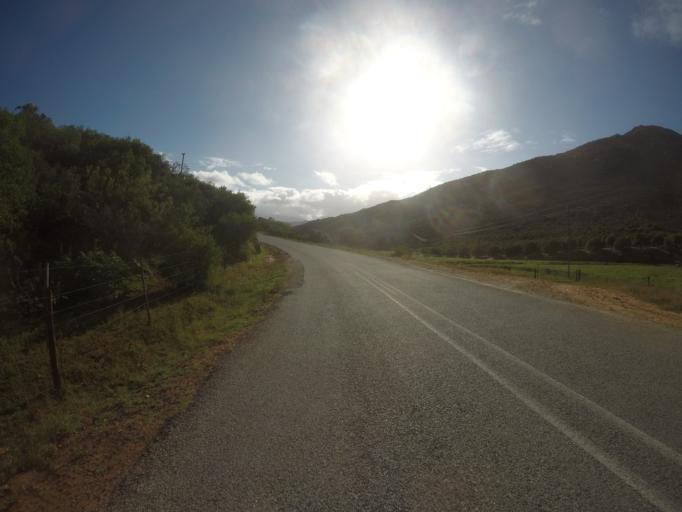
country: ZA
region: Western Cape
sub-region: West Coast District Municipality
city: Clanwilliam
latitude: -32.4376
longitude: 18.9449
